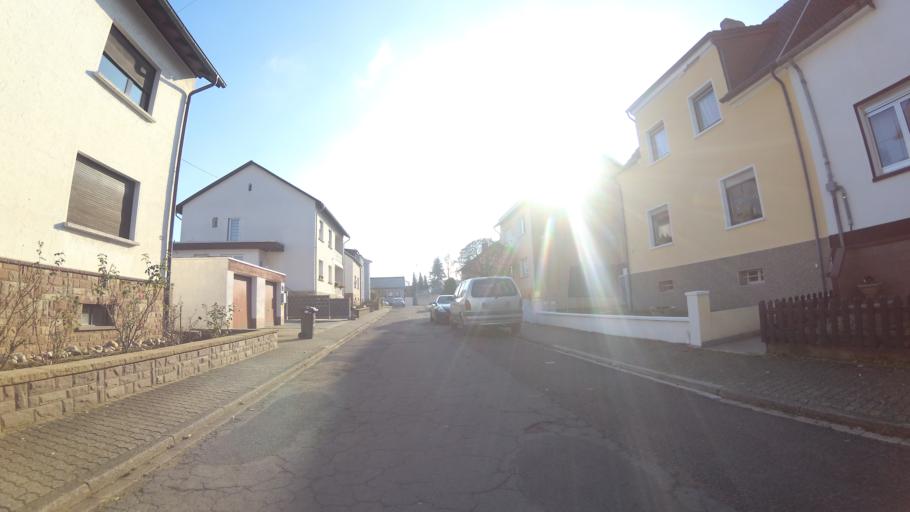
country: DE
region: Saarland
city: Ensdorf
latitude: 49.3130
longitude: 6.7781
